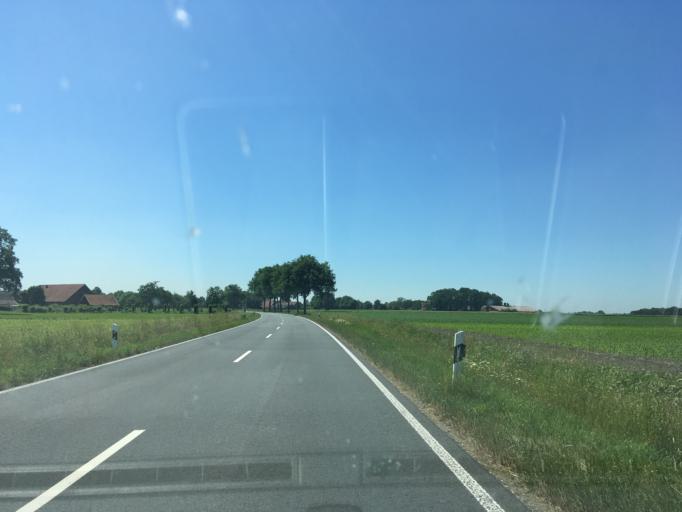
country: DE
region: North Rhine-Westphalia
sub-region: Regierungsbezirk Munster
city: Raesfeld
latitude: 51.7956
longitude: 6.8132
